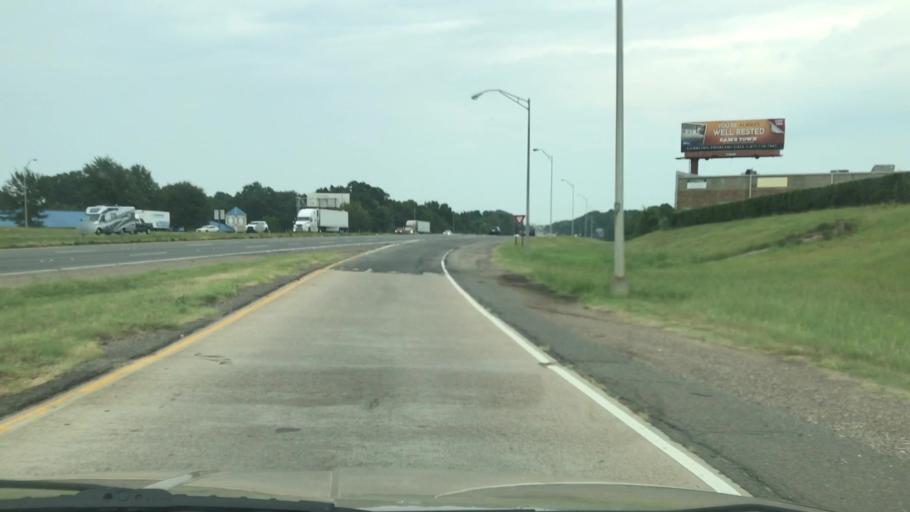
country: US
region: Louisiana
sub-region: Caddo Parish
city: Shreveport
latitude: 32.4617
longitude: -93.8261
